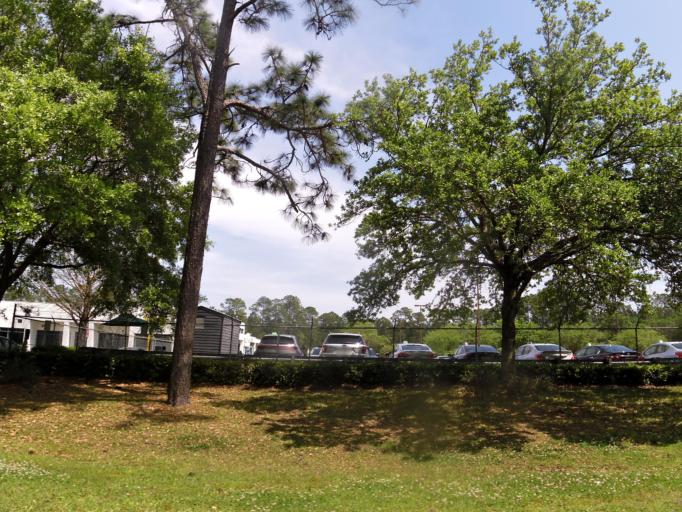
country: US
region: Florida
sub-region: Nassau County
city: Nassau Village-Ratliff
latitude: 30.4932
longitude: -81.6676
